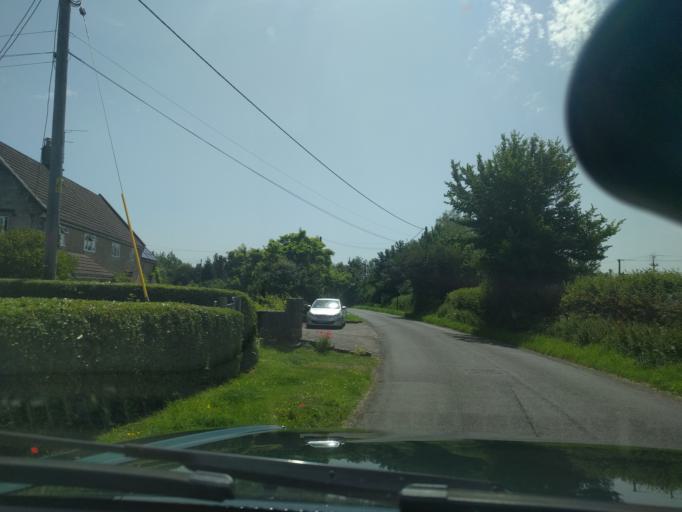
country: GB
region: England
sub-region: Wiltshire
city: Box
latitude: 51.3813
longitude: -2.2423
